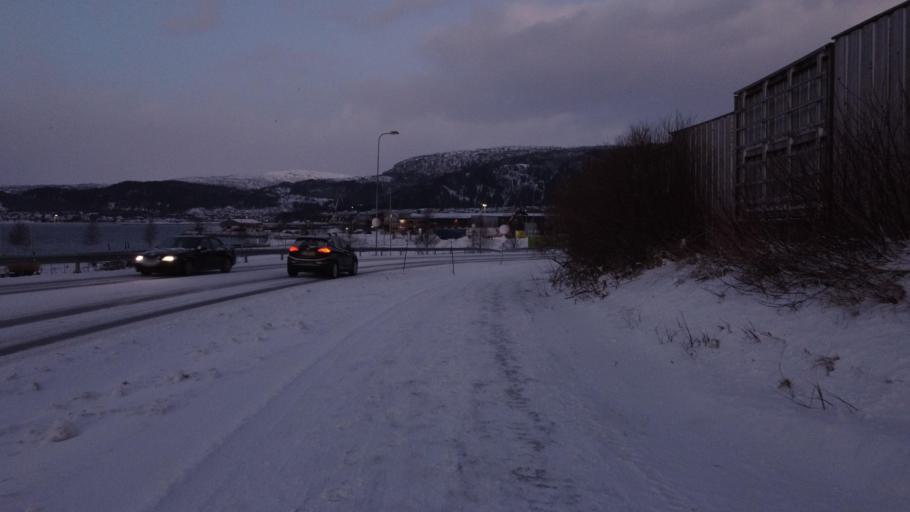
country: NO
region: Nordland
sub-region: Rana
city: Mo i Rana
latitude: 66.3168
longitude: 14.1324
